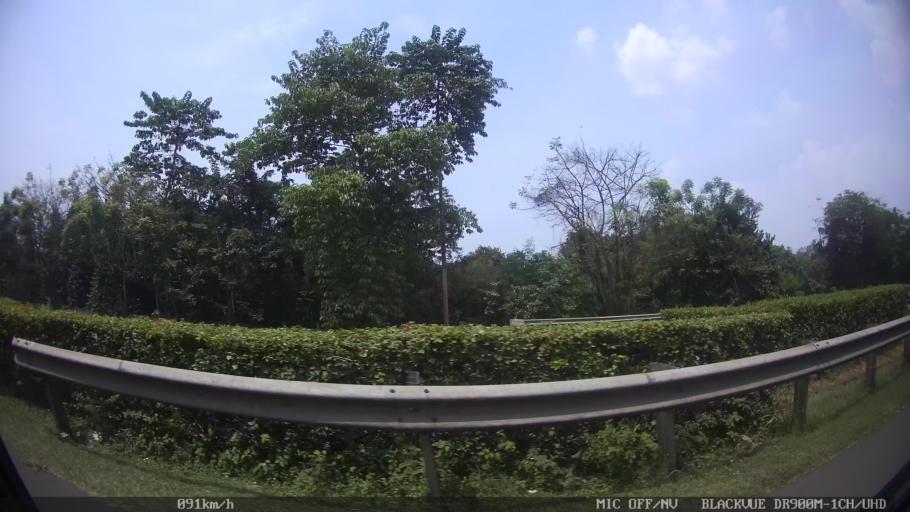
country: ID
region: Banten
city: Serang
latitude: -6.0742
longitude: 106.1300
